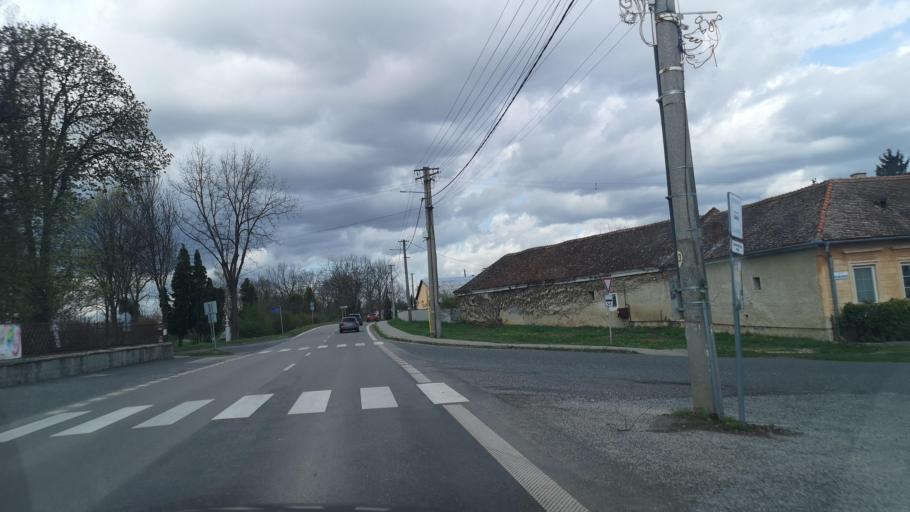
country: SK
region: Nitriansky
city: Zlate Moravce
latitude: 48.3391
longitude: 18.3575
